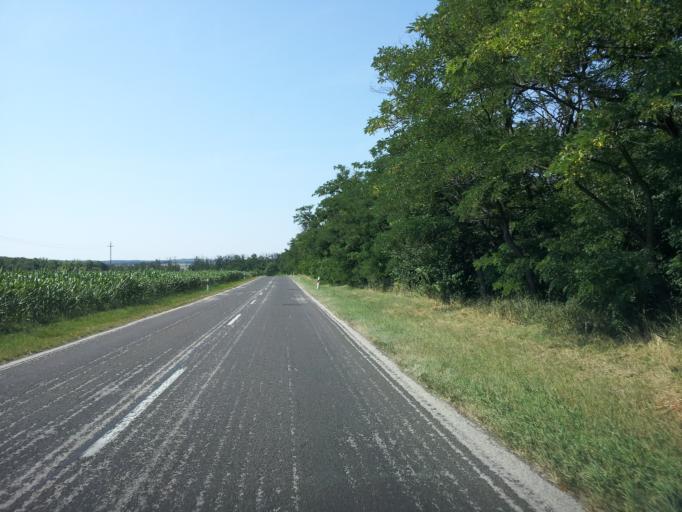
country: HU
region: Fejer
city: Lovasbereny
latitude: 47.2796
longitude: 18.5262
